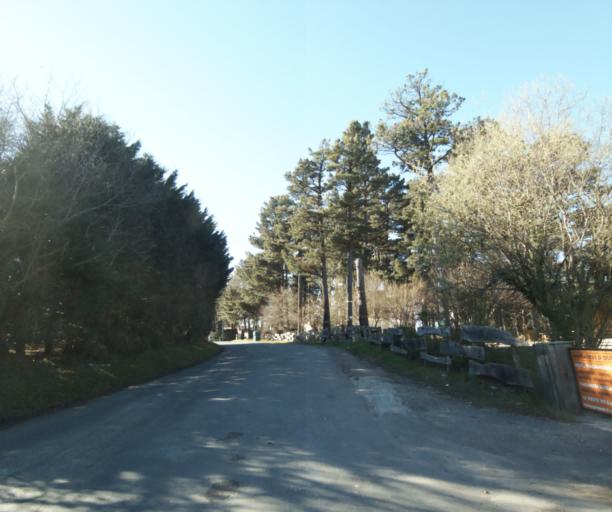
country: FR
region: Aquitaine
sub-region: Departement des Pyrenees-Atlantiques
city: Hendaye
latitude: 43.3565
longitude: -1.7429
